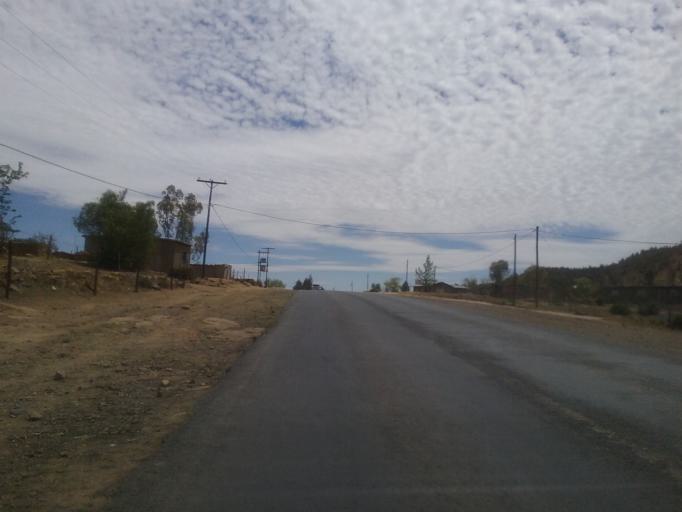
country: LS
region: Mafeteng
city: Mafeteng
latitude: -29.8379
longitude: 27.2328
